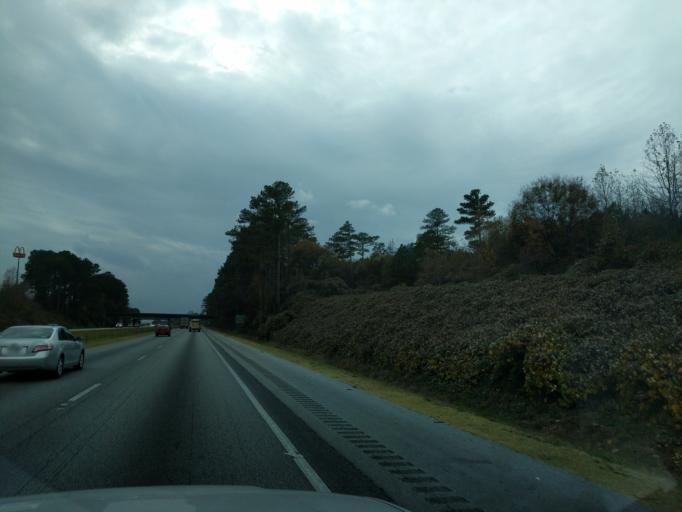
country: US
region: Georgia
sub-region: Franklin County
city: Lavonia
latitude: 34.4496
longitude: -83.1155
